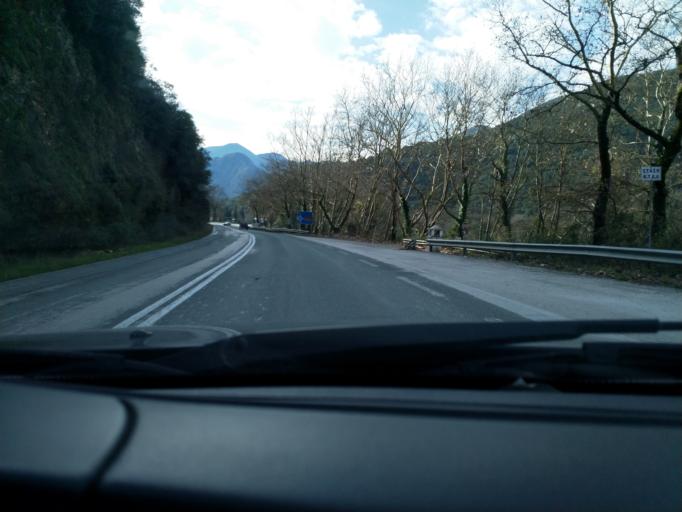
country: GR
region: Epirus
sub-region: Nomos Ioanninon
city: Agia Kyriaki
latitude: 39.4257
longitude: 20.8443
